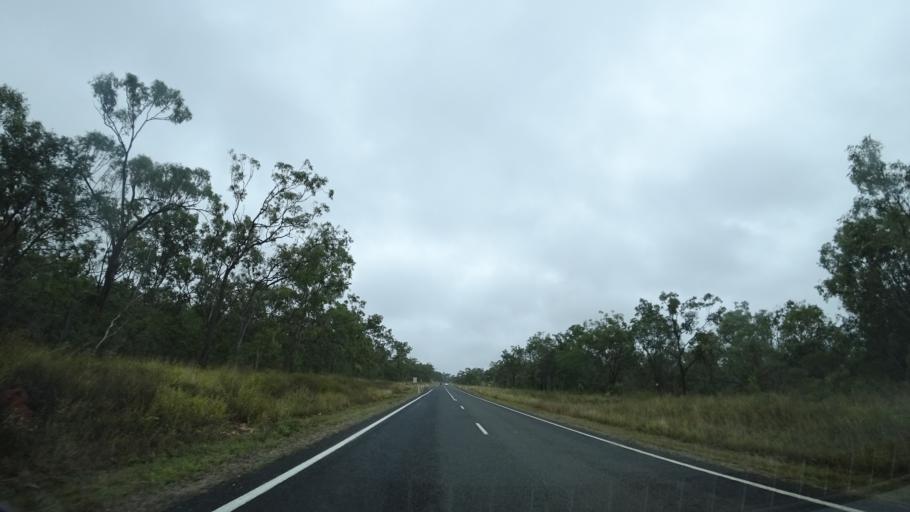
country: AU
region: Queensland
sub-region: Tablelands
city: Ravenshoe
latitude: -17.6819
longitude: 145.1303
